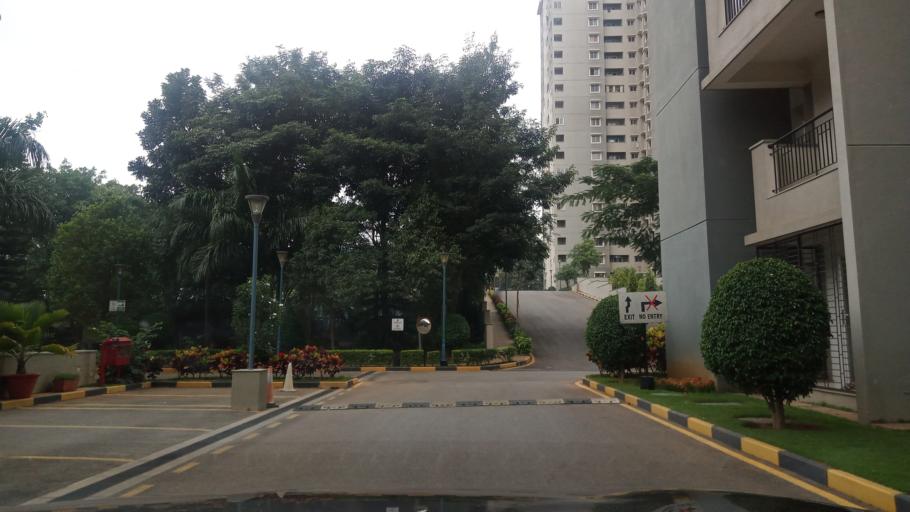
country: IN
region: Karnataka
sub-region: Bangalore Urban
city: Yelahanka
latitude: 13.0458
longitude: 77.5000
